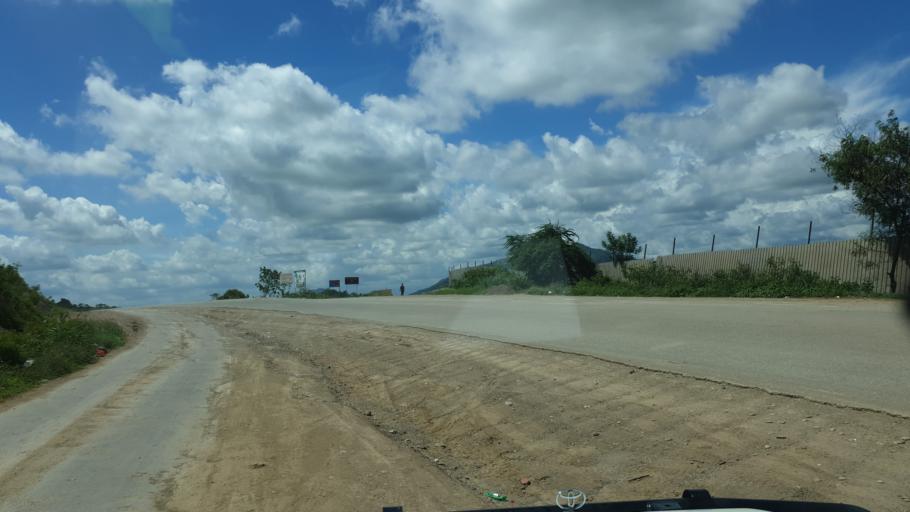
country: PG
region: National Capital
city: Port Moresby
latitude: -9.3976
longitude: 147.2297
